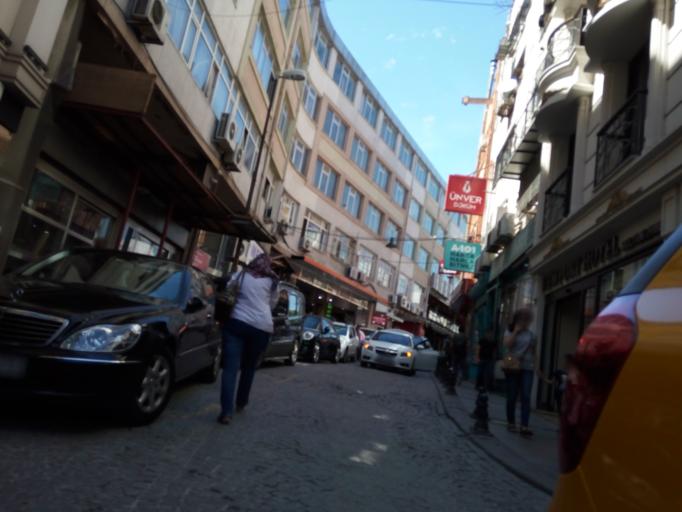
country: TR
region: Istanbul
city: Eminoenue
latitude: 41.0075
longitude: 28.9717
